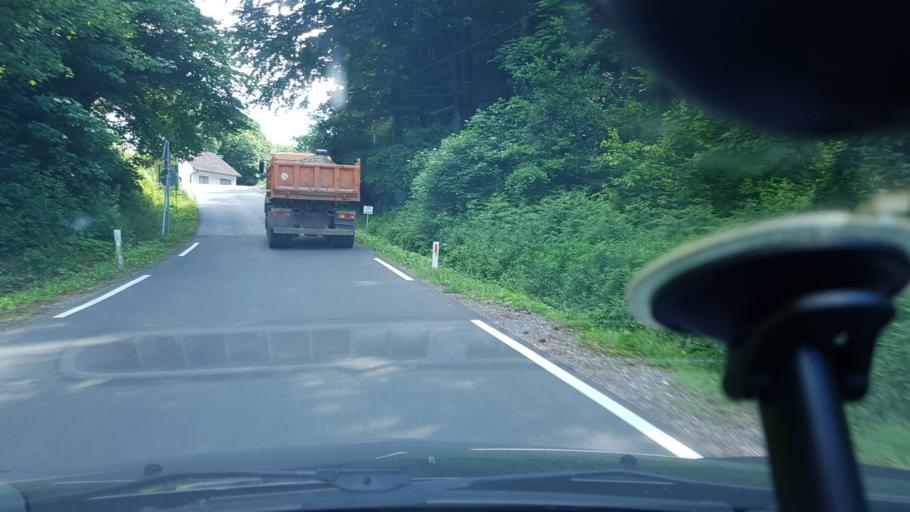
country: SI
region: Rogatec
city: Rogatec
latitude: 46.2594
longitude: 15.7595
